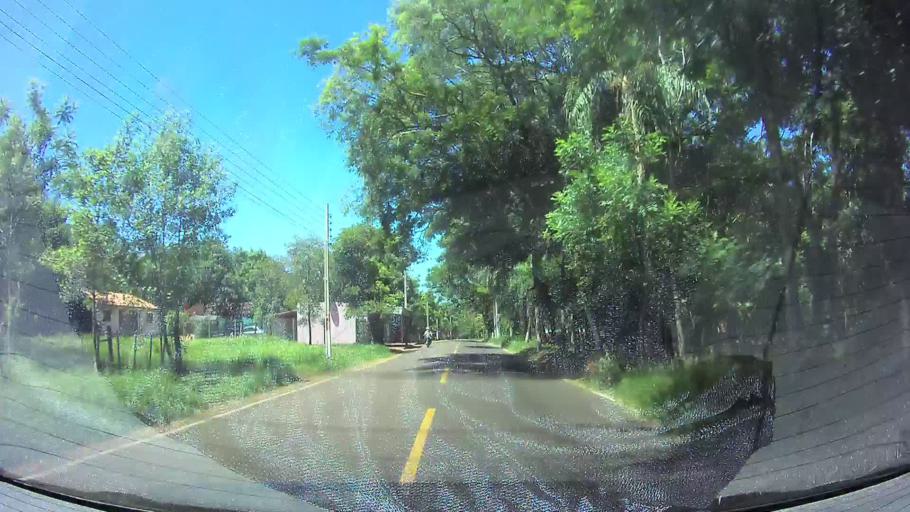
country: PY
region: Central
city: Aregua
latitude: -25.2507
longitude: -57.4414
